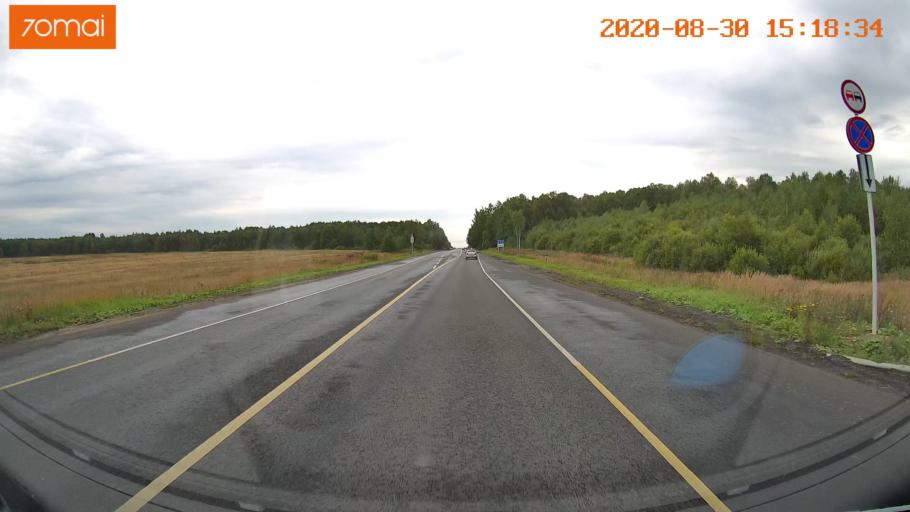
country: RU
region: Ivanovo
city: Rodniki
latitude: 57.1216
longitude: 41.7922
